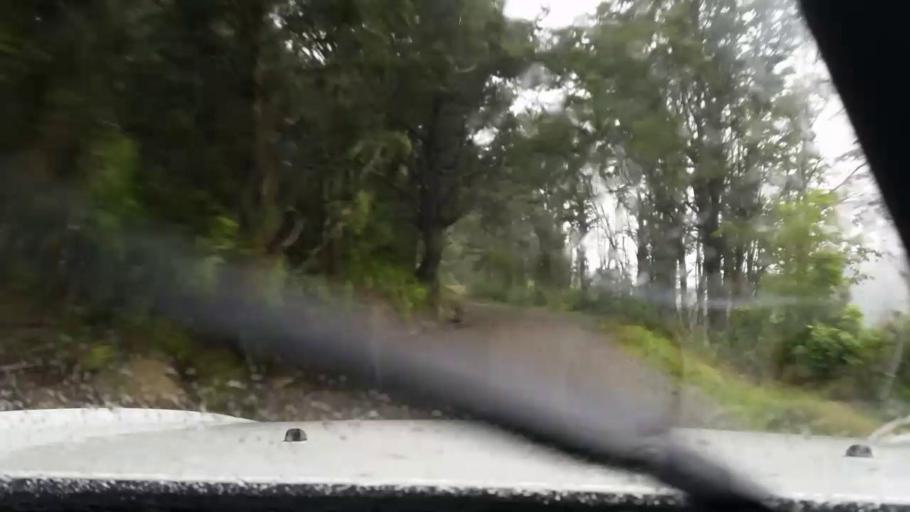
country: NZ
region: Wellington
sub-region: Masterton District
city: Masterton
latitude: -41.1843
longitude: 175.8228
